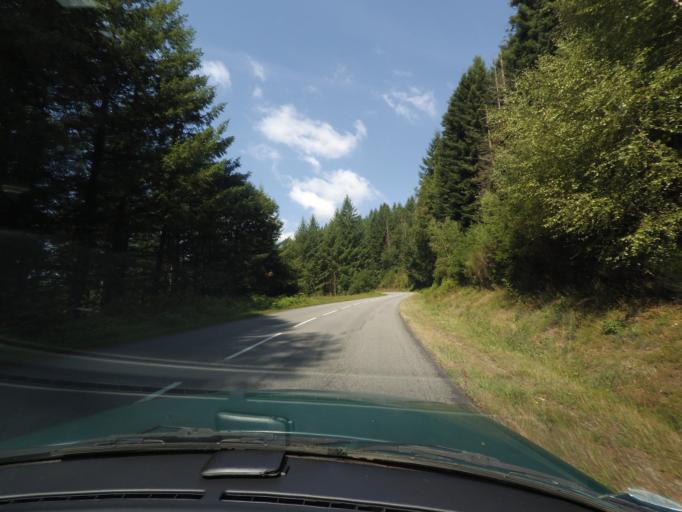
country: FR
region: Limousin
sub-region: Departement de la Haute-Vienne
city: Eymoutiers
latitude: 45.7235
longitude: 1.8001
